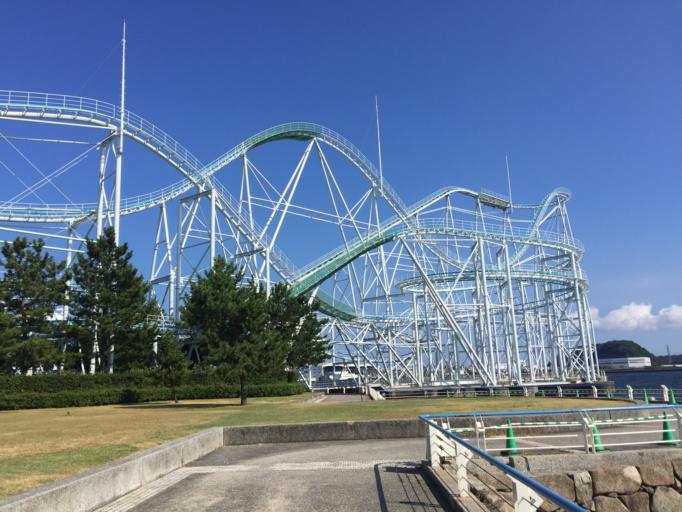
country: JP
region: Kanagawa
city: Yokosuka
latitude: 35.3348
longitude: 139.6428
